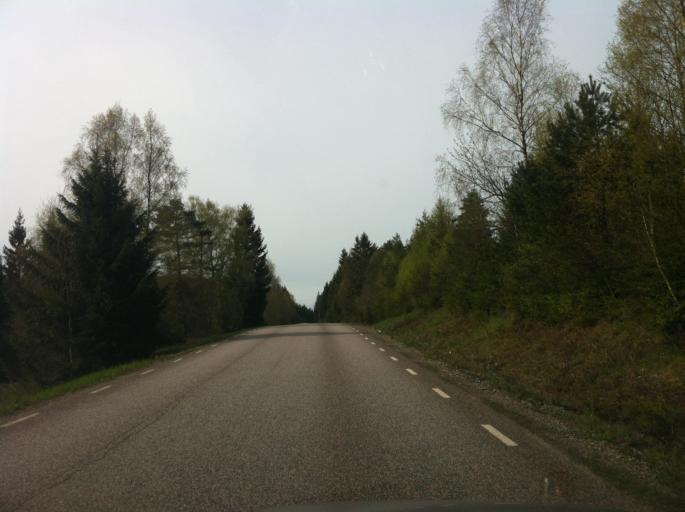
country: SE
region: Vaestra Goetaland
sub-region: Bollebygds Kommun
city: Bollebygd
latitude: 57.6465
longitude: 12.6189
